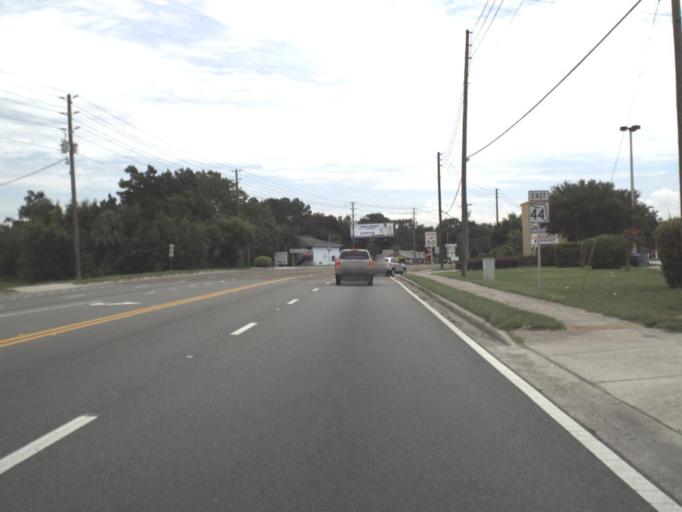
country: US
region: Florida
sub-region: Citrus County
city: Crystal River
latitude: 28.8911
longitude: -82.5484
